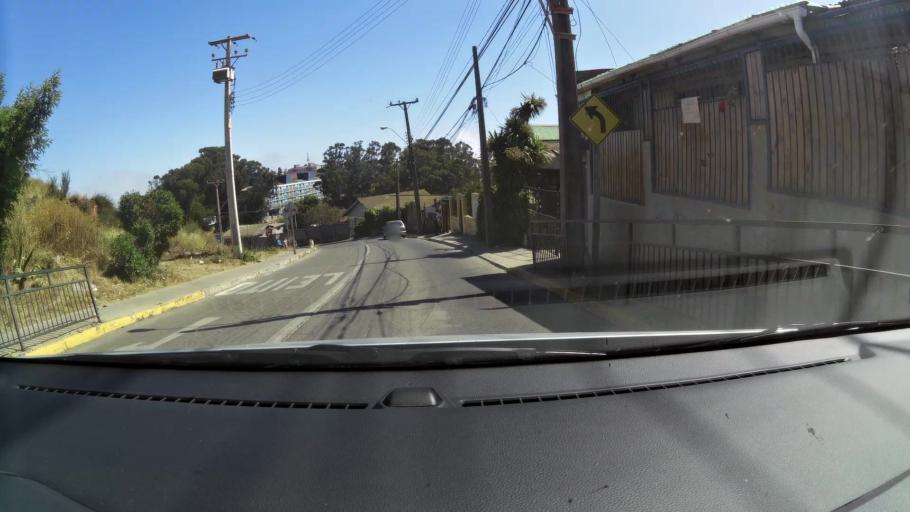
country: CL
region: Valparaiso
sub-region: Provincia de Valparaiso
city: Valparaiso
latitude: -33.0446
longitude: -71.6465
